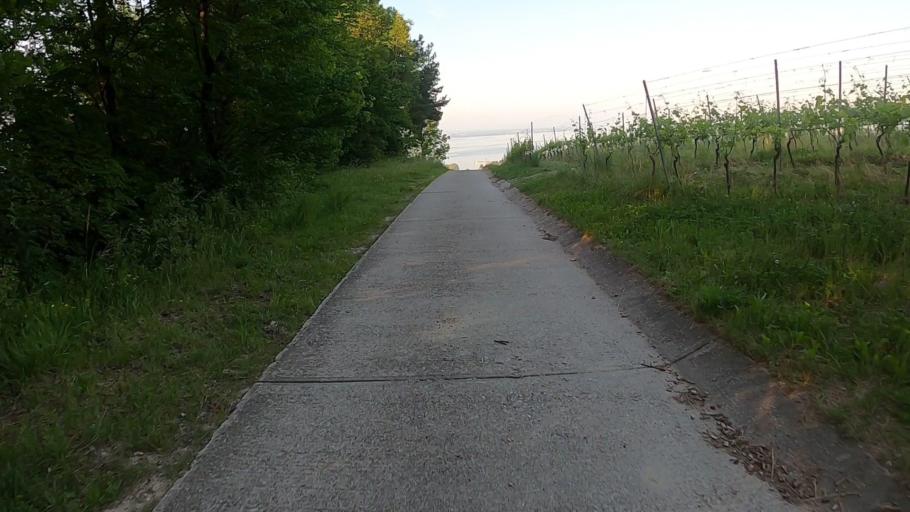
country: CH
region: Vaud
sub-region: Nyon District
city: Rolle
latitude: 46.4766
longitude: 6.3434
